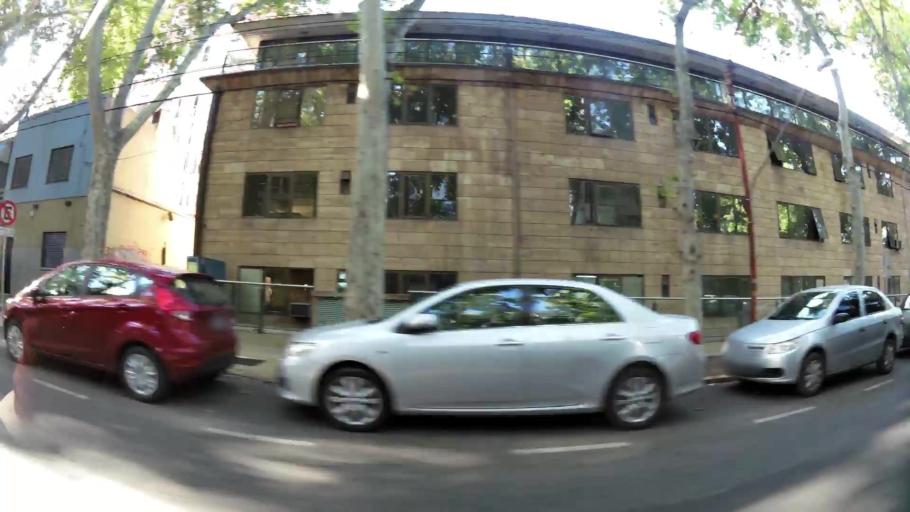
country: AR
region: Mendoza
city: Mendoza
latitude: -32.8917
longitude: -68.8456
